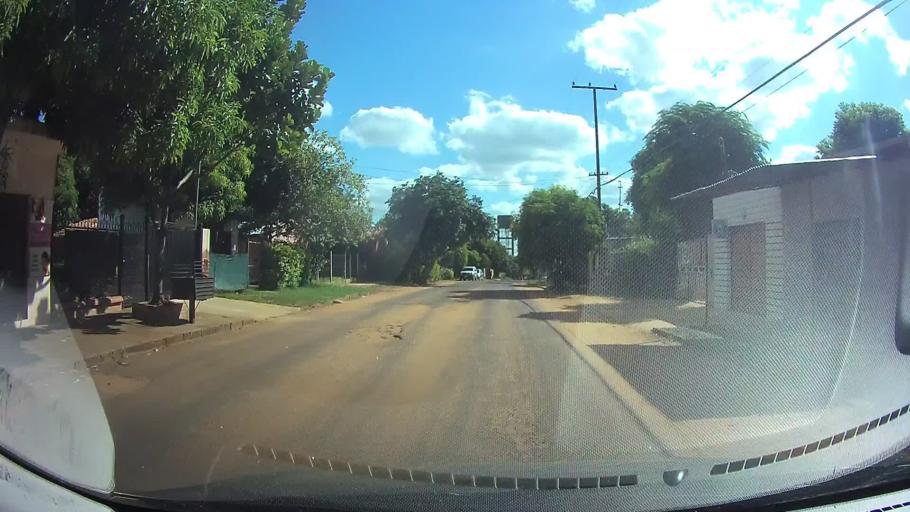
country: PY
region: Central
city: Itaugua
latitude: -25.3869
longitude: -57.3470
